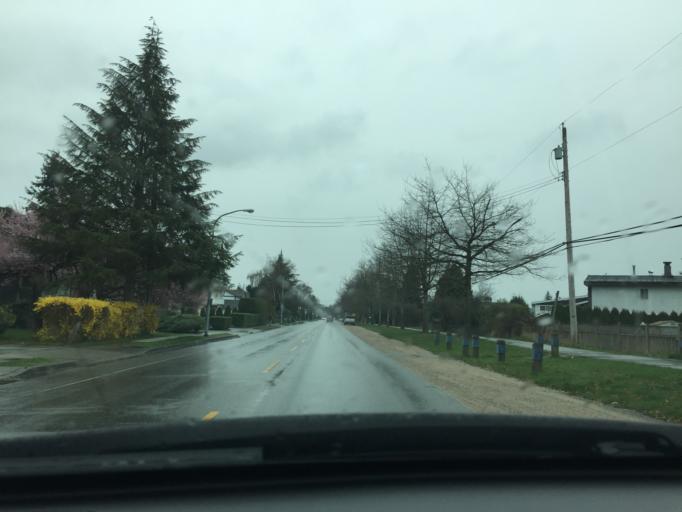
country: CA
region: British Columbia
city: Richmond
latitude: 49.1472
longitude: -123.1252
